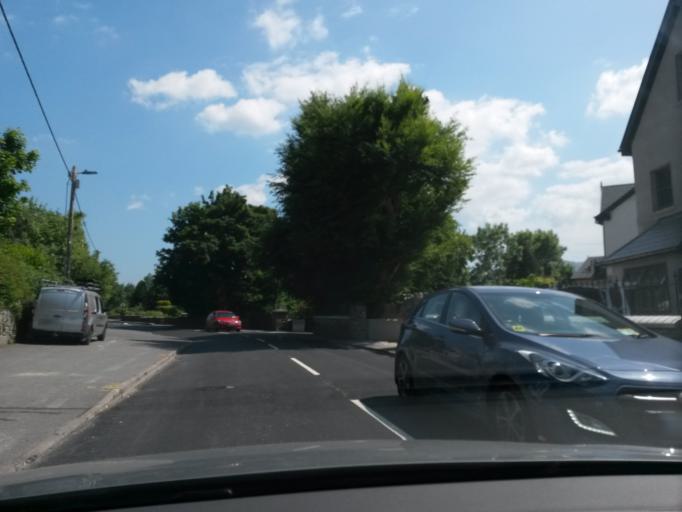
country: IE
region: Munster
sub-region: Ciarrai
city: Cill Airne
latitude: 52.0516
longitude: -9.5053
